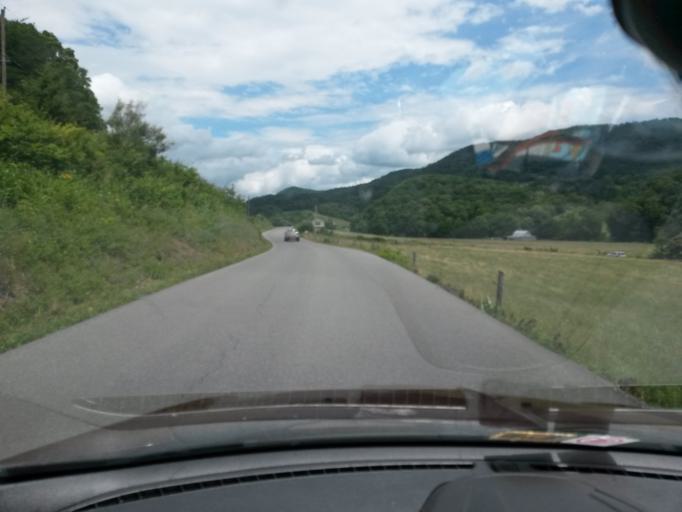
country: US
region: West Virginia
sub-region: Monroe County
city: Union
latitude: 37.5011
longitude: -80.5921
